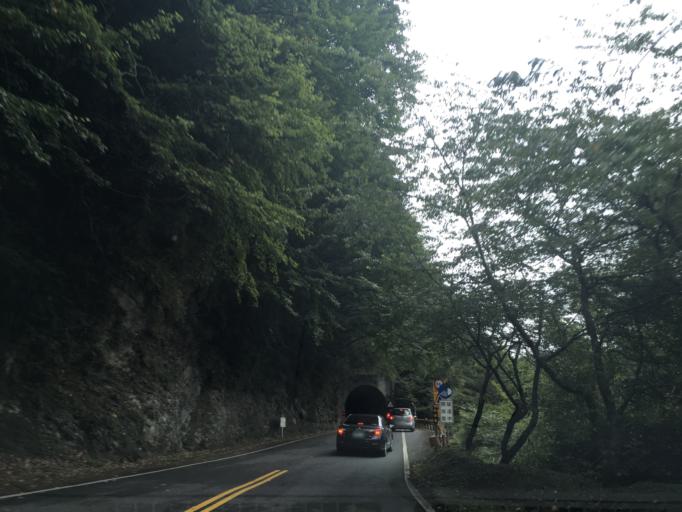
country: TW
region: Taiwan
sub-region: Hualien
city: Hualian
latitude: 24.1894
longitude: 121.3468
